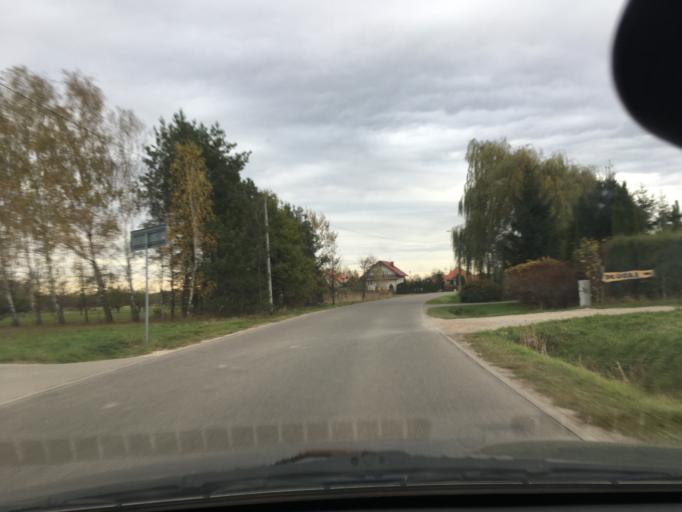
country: PL
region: Lodz Voivodeship
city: Zabia Wola
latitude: 52.0100
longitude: 20.6950
